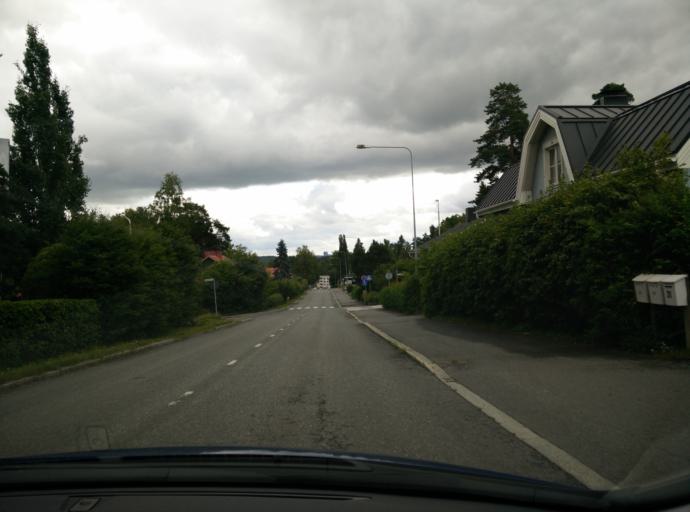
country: FI
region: Haeme
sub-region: Haemeenlinna
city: Haemeenlinna
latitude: 60.9867
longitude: 24.4513
